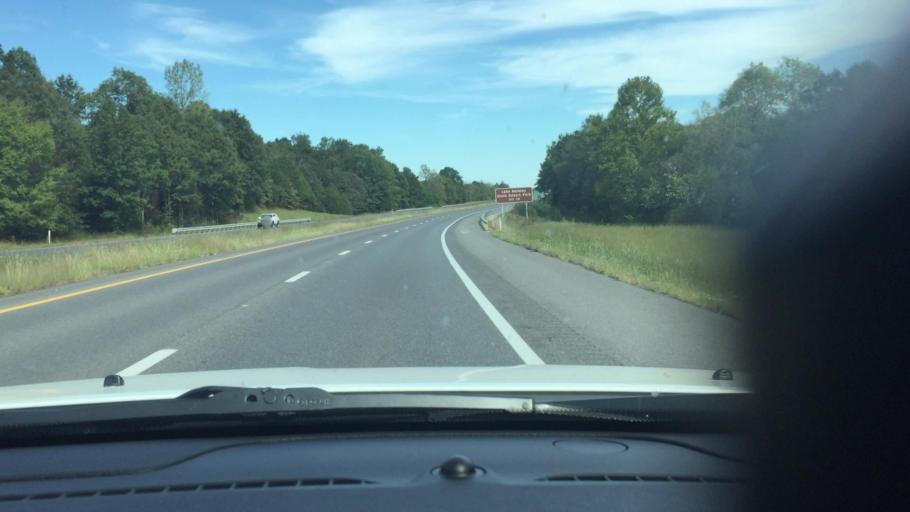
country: US
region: Kentucky
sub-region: Caldwell County
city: Princeton
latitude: 37.1172
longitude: -87.9213
